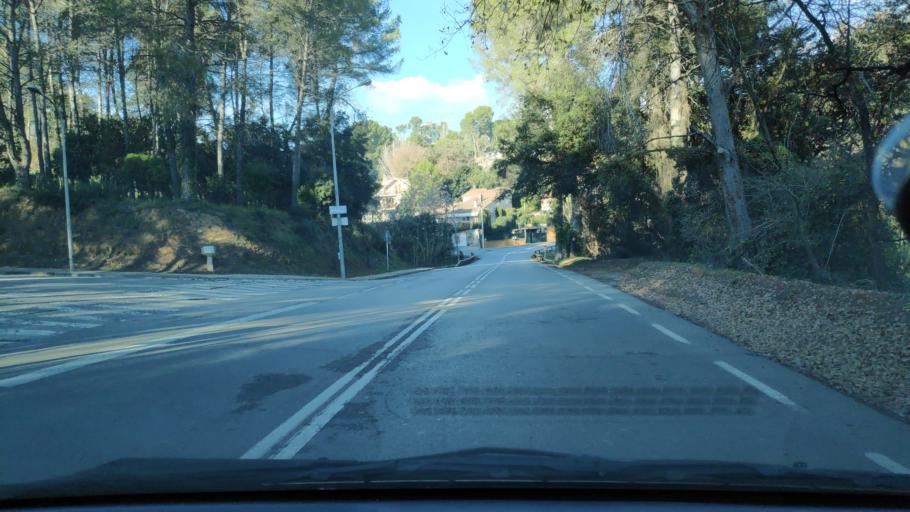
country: ES
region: Catalonia
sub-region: Provincia de Barcelona
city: Sant Cugat del Valles
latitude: 41.4999
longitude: 2.0871
